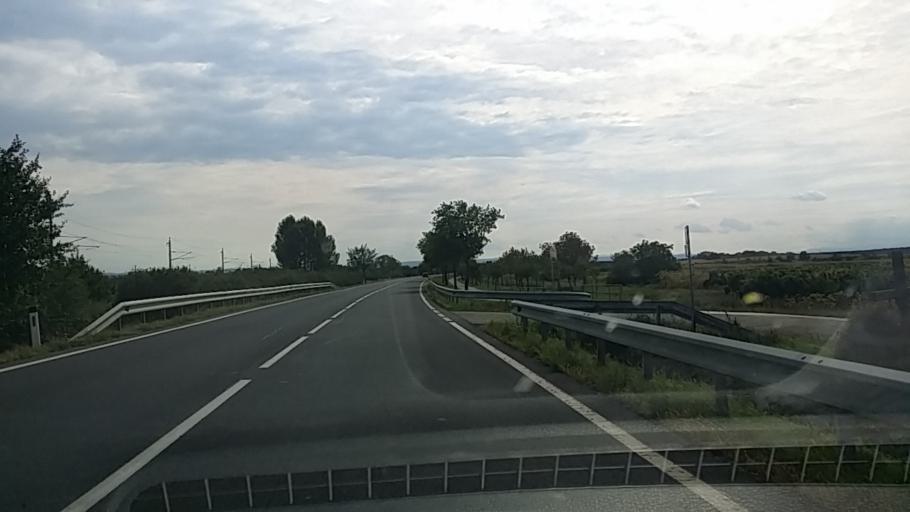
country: AT
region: Burgenland
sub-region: Eisenstadt-Umgebung
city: Schutzen am Gebirge
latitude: 47.8614
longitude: 16.6440
